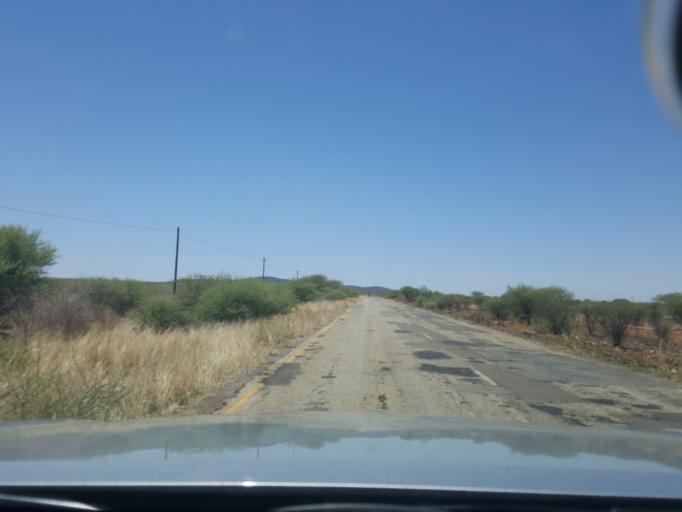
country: BW
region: South East
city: Ramotswa
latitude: -25.0737
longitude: 25.9496
